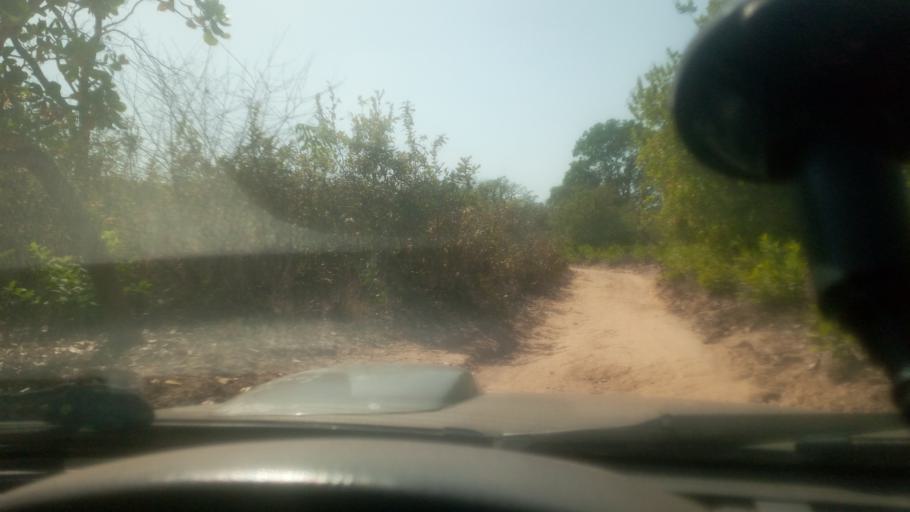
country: GW
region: Oio
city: Farim
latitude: 12.4533
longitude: -15.4177
